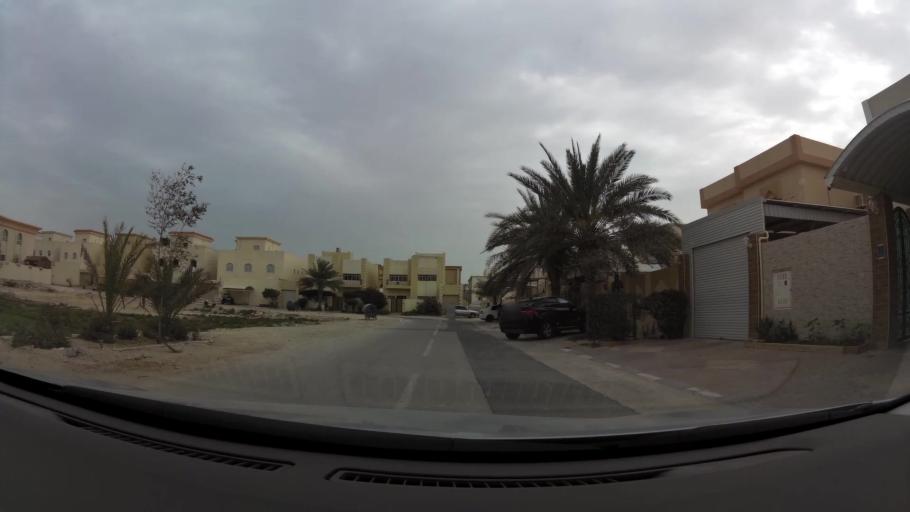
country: QA
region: Baladiyat ar Rayyan
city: Ar Rayyan
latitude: 25.3412
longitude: 51.4744
